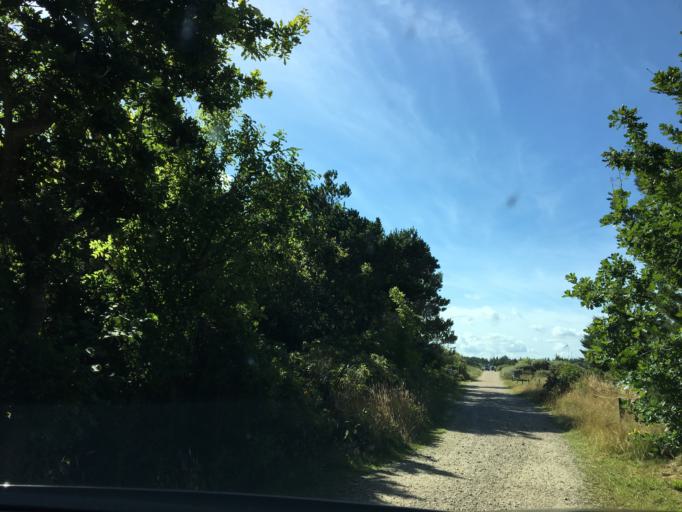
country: DK
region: Central Jutland
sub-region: Ringkobing-Skjern Kommune
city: Hvide Sande
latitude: 55.8655
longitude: 8.1739
